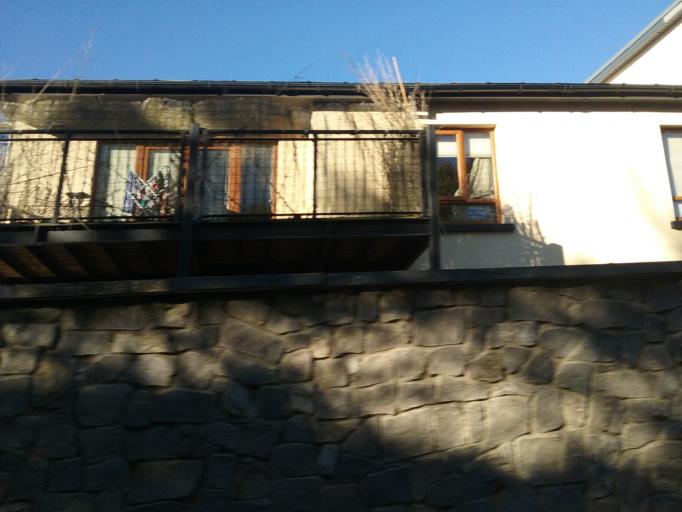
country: IE
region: Leinster
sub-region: Lu
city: Drogheda
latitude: 53.7145
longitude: -6.3802
